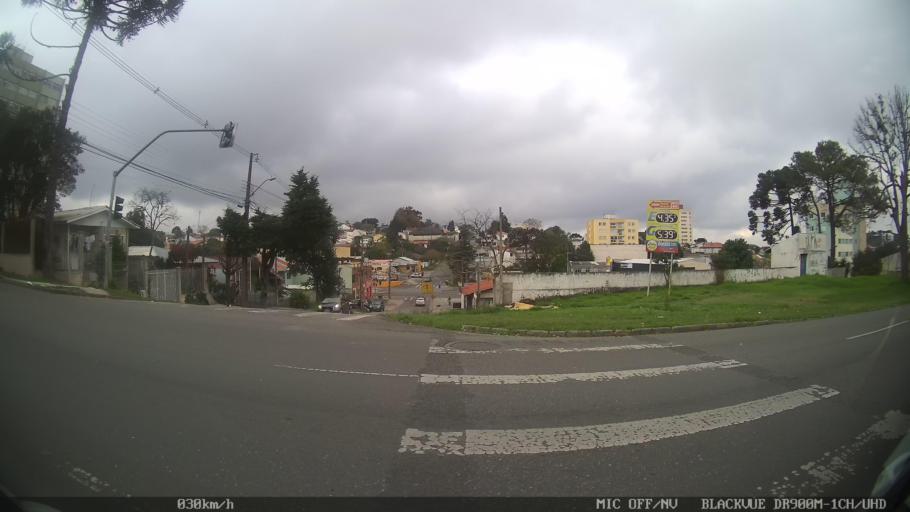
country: BR
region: Parana
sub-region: Curitiba
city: Curitiba
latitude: -25.3782
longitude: -49.2278
